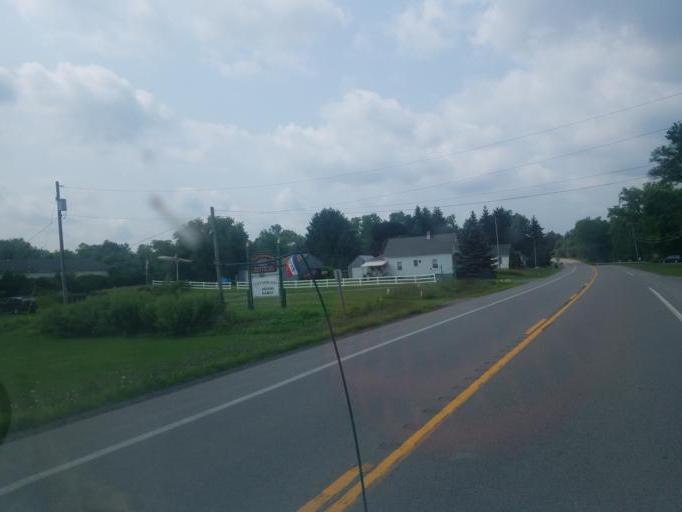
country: US
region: New York
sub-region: Herkimer County
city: Herkimer
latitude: 43.0182
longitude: -74.9594
